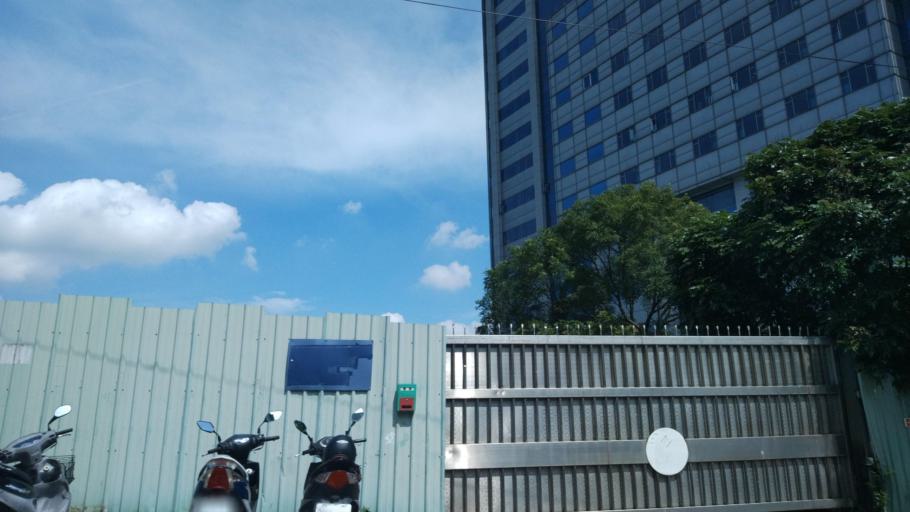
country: TW
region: Taipei
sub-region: Taipei
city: Banqiao
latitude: 24.9531
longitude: 121.5045
